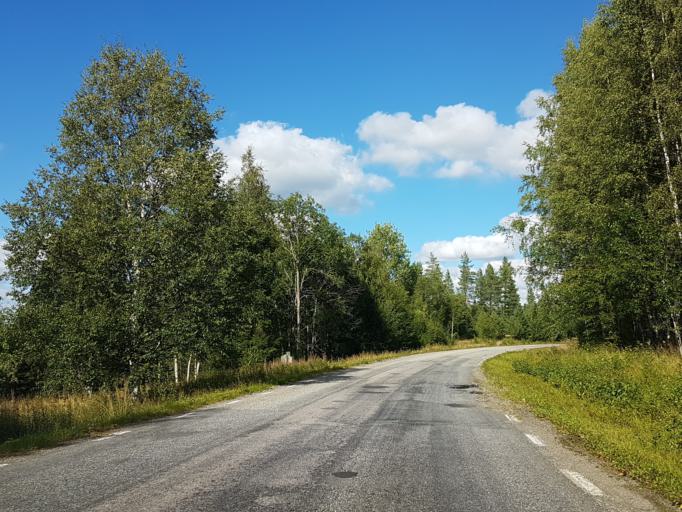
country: SE
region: Vaesterbotten
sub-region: Skelleftea Kommun
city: Burtraesk
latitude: 64.2382
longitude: 20.4790
